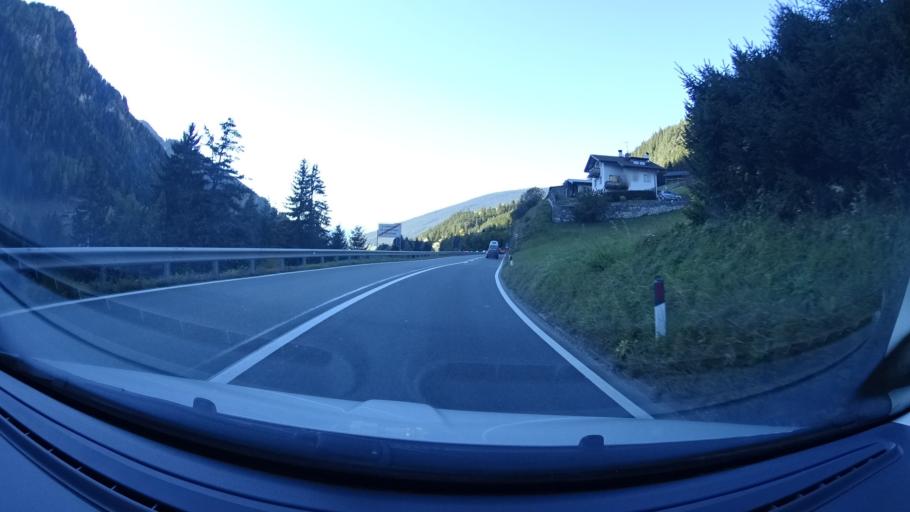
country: IT
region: Trentino-Alto Adige
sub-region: Bolzano
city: Santa Cristina Valgardena
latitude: 46.5616
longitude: 11.7037
